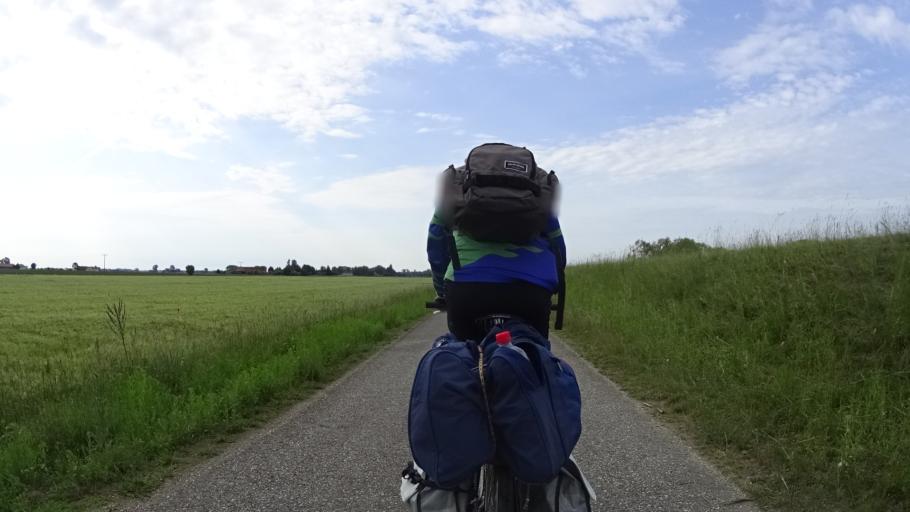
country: DE
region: Bavaria
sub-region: Lower Bavaria
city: Irlbach
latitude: 48.8580
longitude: 12.7645
